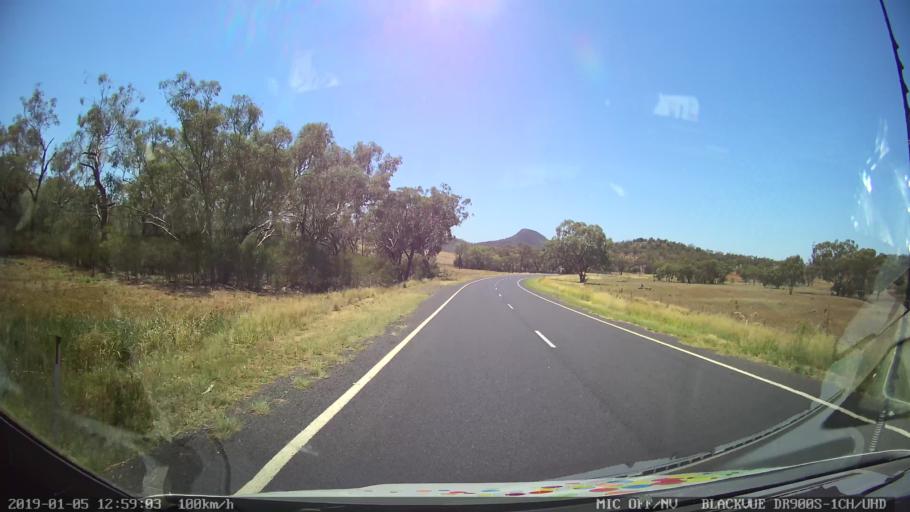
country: AU
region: New South Wales
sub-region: Narrabri
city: Boggabri
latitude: -31.1124
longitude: 149.7596
